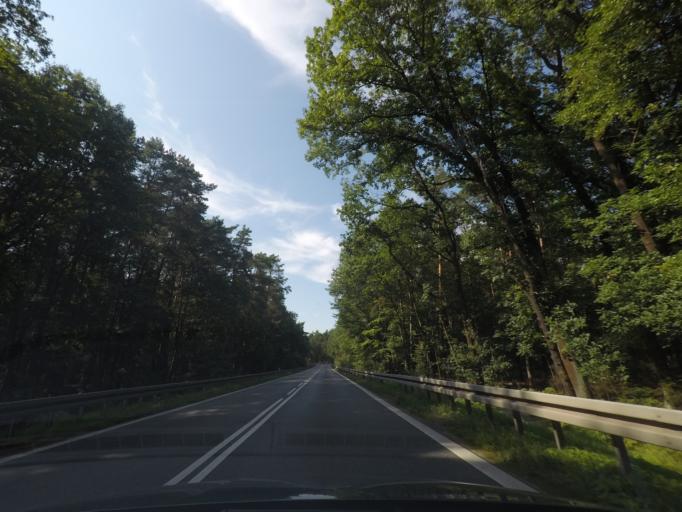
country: PL
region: Silesian Voivodeship
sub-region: Powiat pszczynski
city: Radostowice
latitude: 50.0181
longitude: 18.8489
